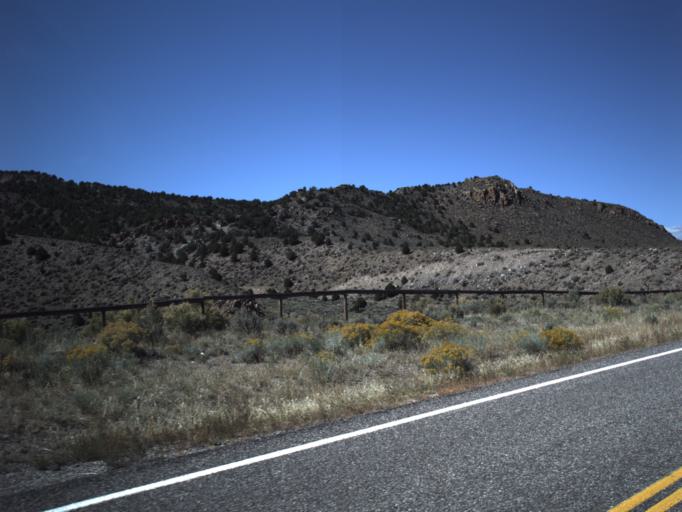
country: US
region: Utah
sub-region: Piute County
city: Junction
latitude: 38.1787
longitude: -112.0781
